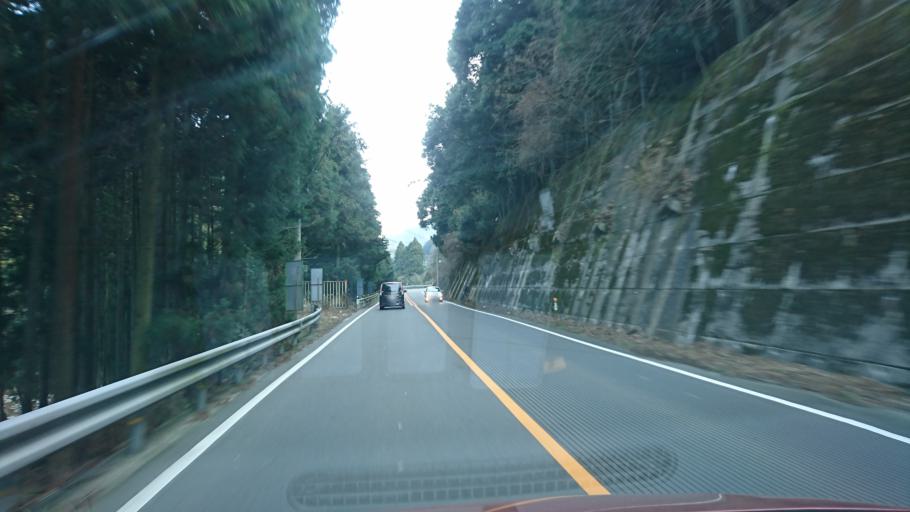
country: JP
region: Ehime
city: Hojo
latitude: 33.9663
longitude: 132.9052
